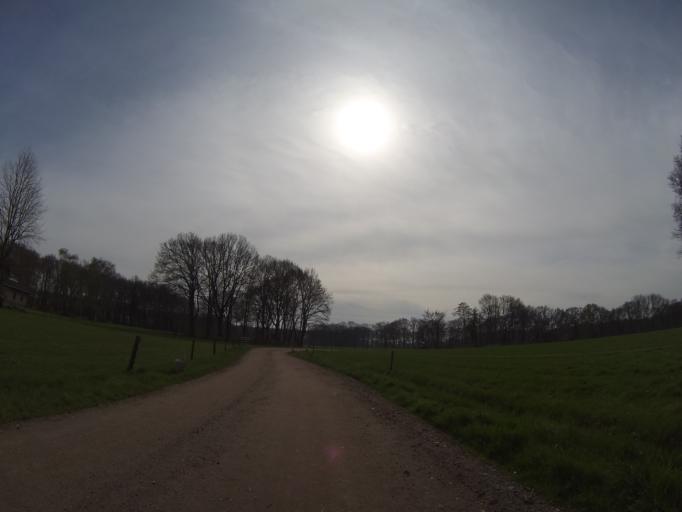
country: NL
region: Gelderland
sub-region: Gemeente Barneveld
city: Terschuur
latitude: 52.1870
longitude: 5.5492
